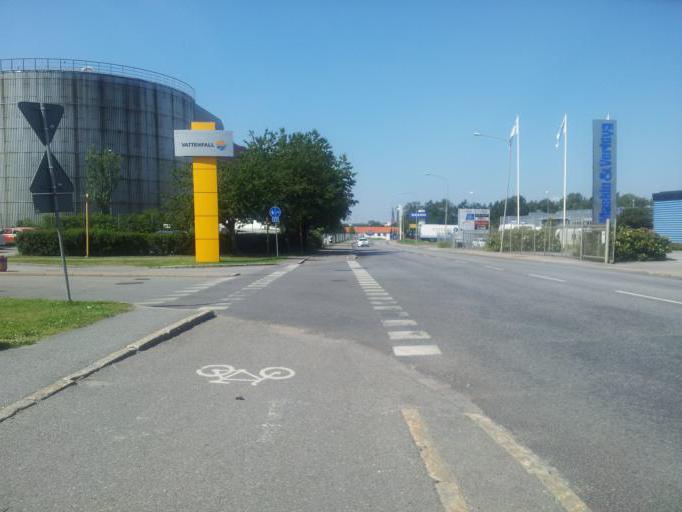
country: SE
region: Uppsala
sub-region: Uppsala Kommun
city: Uppsala
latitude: 59.8537
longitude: 17.6788
